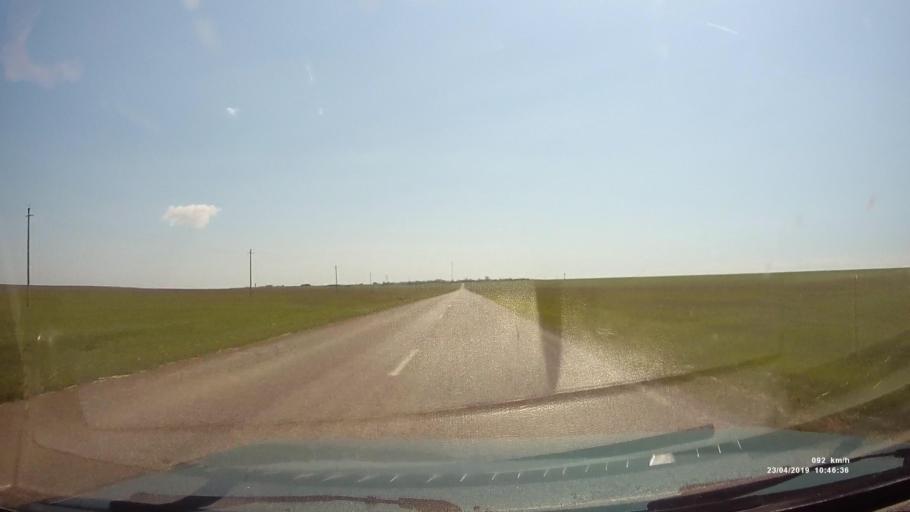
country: RU
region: Kalmykiya
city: Yashalta
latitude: 46.4417
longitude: 42.6938
